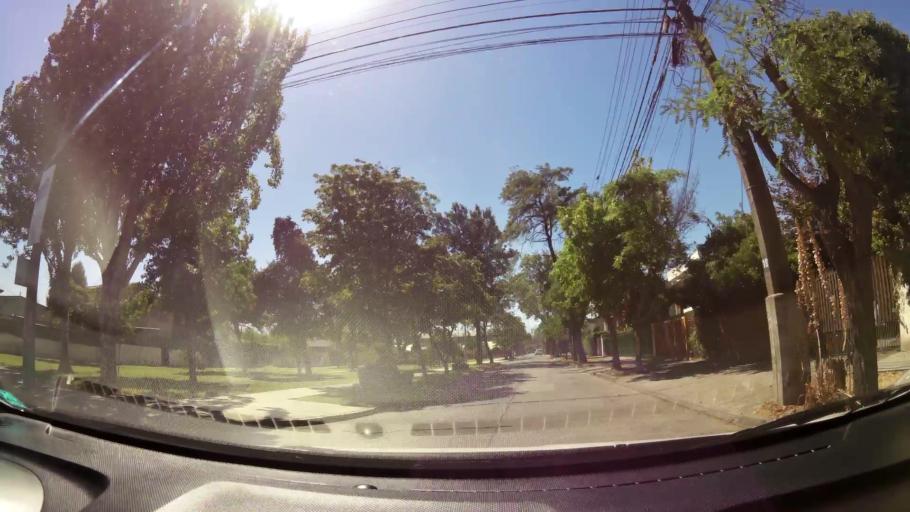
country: CL
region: O'Higgins
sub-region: Provincia de Cachapoal
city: Rancagua
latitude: -34.1736
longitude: -70.7335
